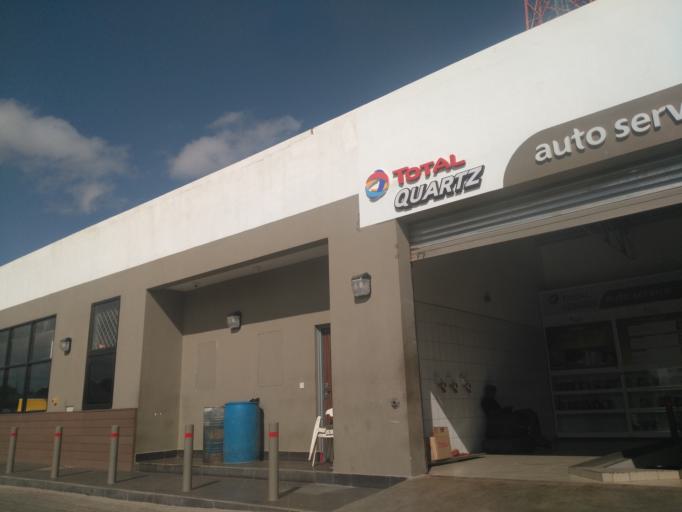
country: TZ
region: Dodoma
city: Dodoma
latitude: -6.1887
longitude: 35.7358
